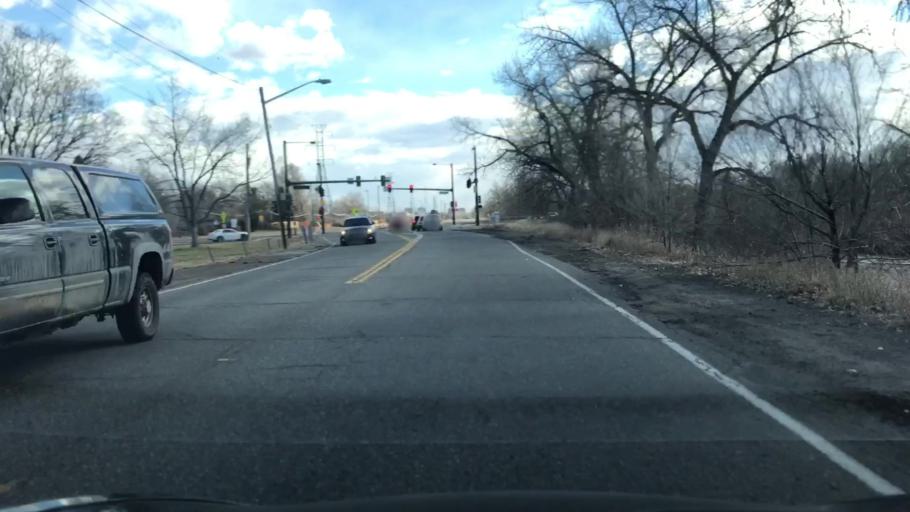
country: US
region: Colorado
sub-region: Arapahoe County
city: Glendale
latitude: 39.6920
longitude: -104.9141
